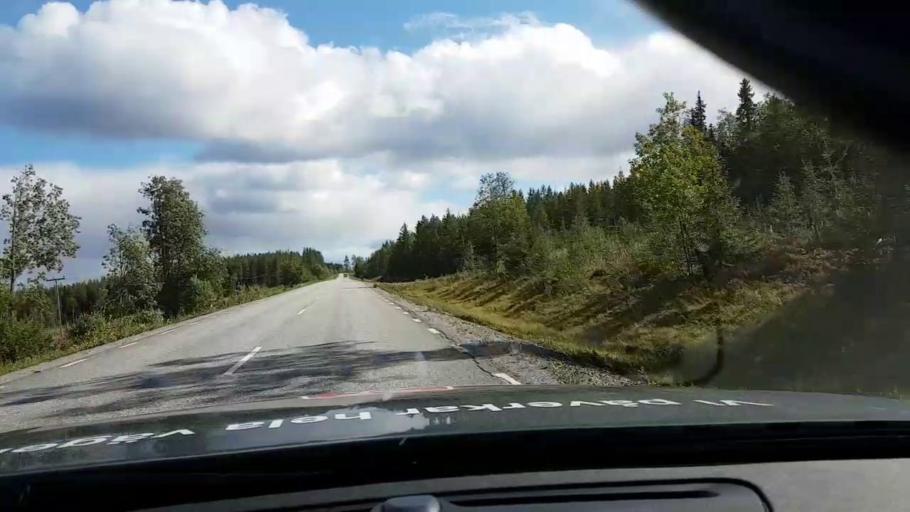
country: SE
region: Vaesterbotten
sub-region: Asele Kommun
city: Asele
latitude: 63.7767
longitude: 17.6708
